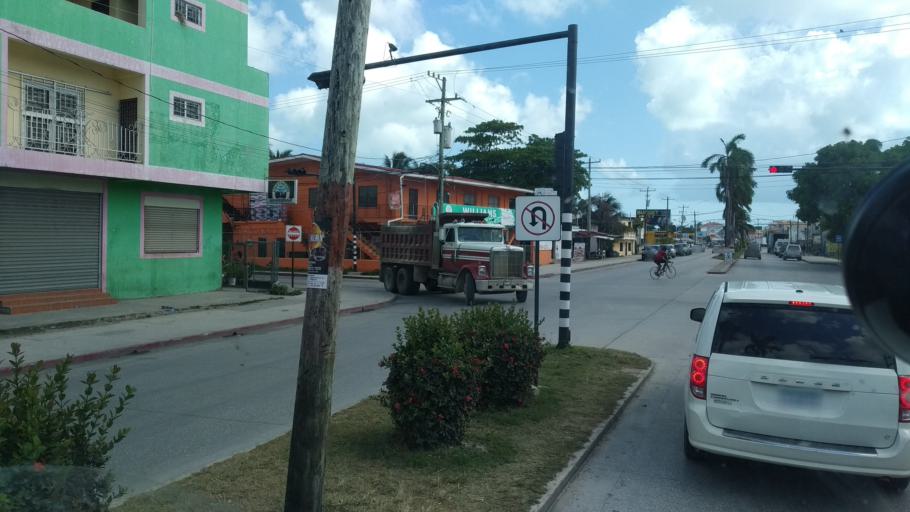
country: BZ
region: Belize
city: Belize City
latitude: 17.4983
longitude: -88.1990
